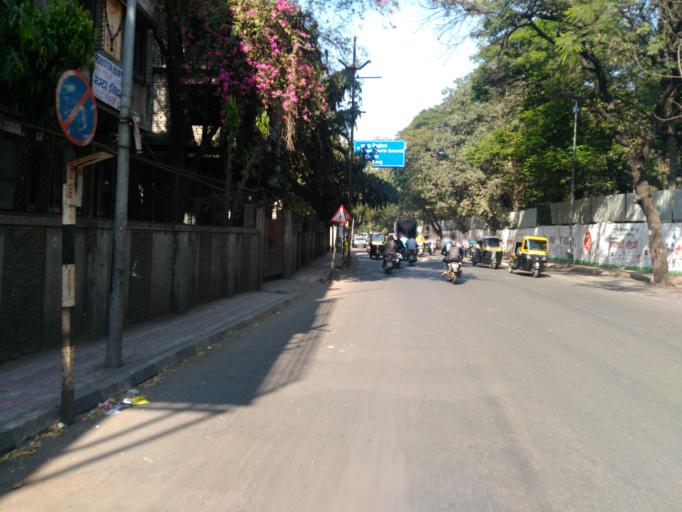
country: IN
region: Maharashtra
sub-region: Pune Division
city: Pune
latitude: 18.5015
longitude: 73.8508
